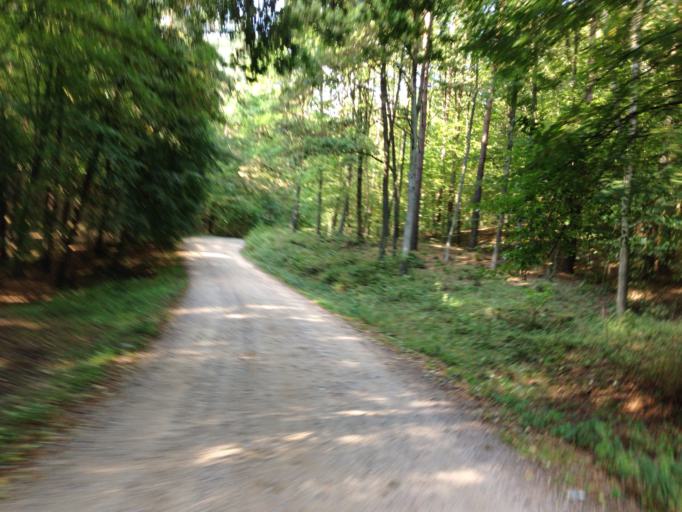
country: PL
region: Kujawsko-Pomorskie
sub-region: Powiat brodnicki
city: Gorzno
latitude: 53.1930
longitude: 19.6625
